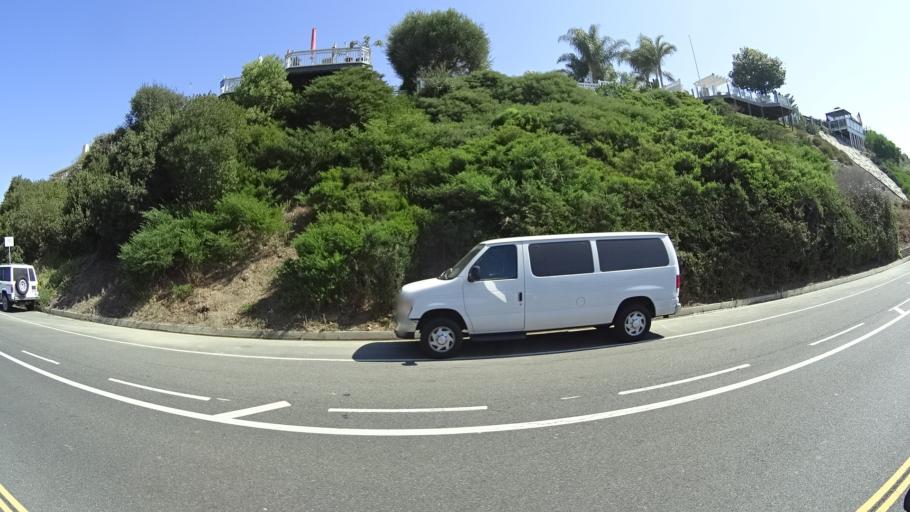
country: US
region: California
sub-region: Orange County
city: San Clemente
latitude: 33.4503
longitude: -117.6457
